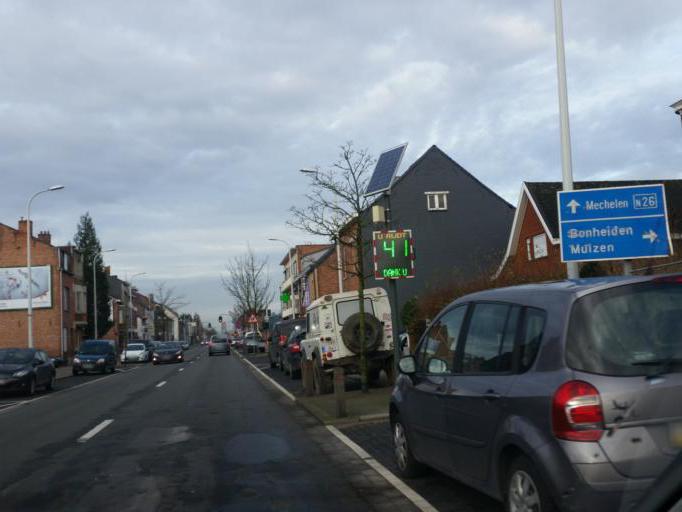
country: BE
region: Flanders
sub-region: Provincie Antwerpen
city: Bonheiden
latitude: 51.0060
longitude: 4.5142
